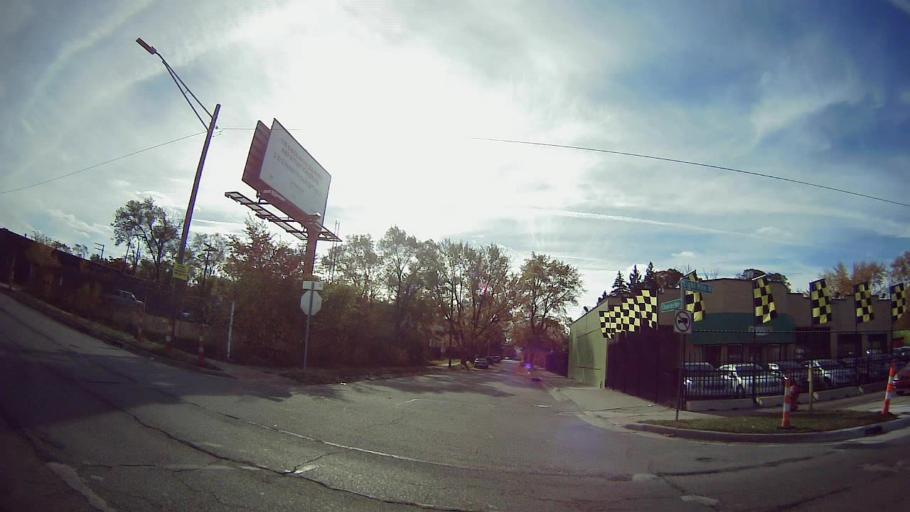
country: US
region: Michigan
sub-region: Oakland County
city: Hazel Park
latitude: 42.4469
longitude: -83.1074
